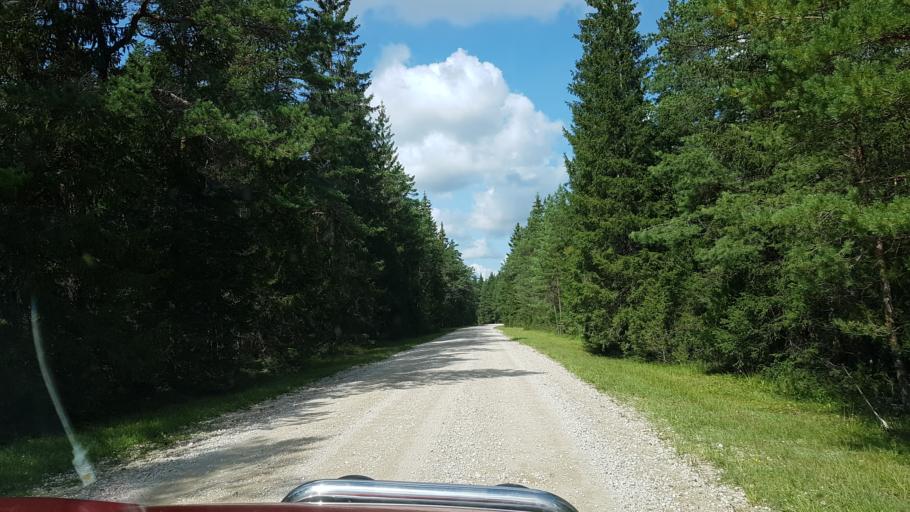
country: EE
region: Raplamaa
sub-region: Rapla vald
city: Rapla
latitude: 58.9640
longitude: 24.6387
